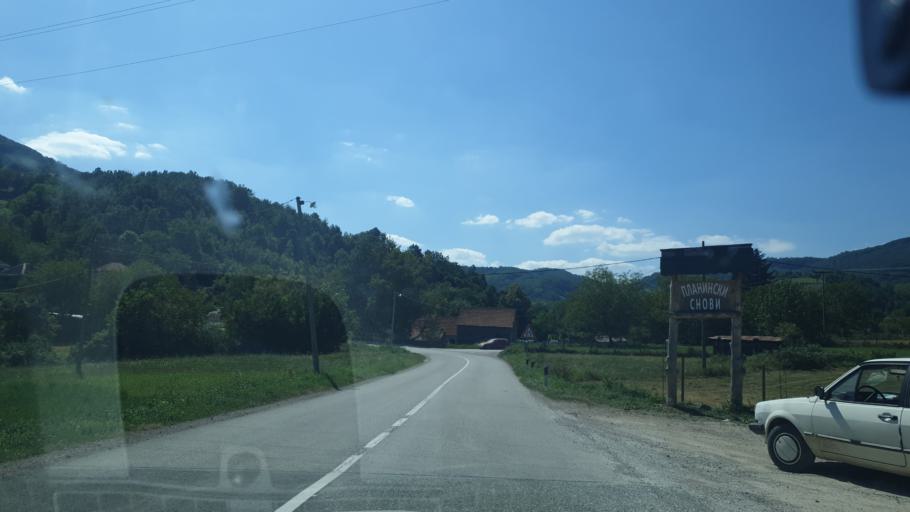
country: RS
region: Central Serbia
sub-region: Kolubarski Okrug
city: Mionica
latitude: 44.1613
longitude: 19.9853
